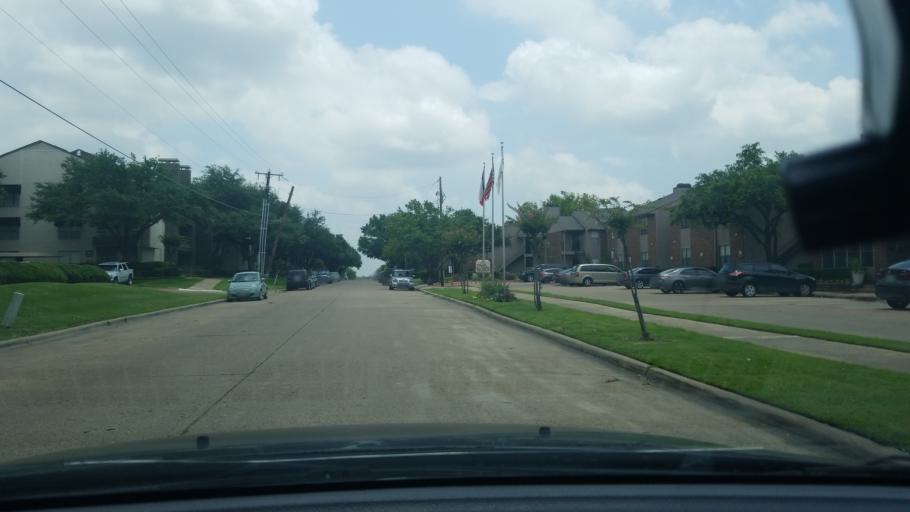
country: US
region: Texas
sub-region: Dallas County
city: Mesquite
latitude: 32.8051
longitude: -96.6184
